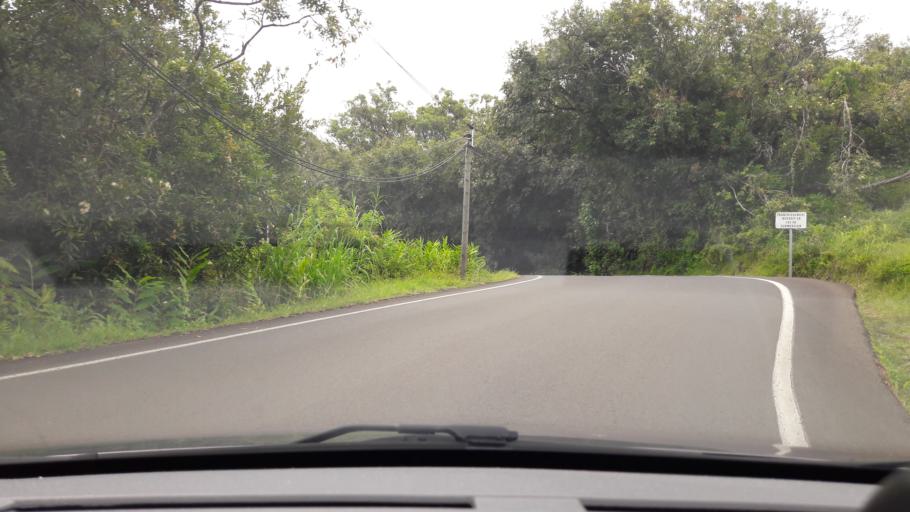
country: RE
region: Reunion
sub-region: Reunion
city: Saint-Benoit
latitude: -21.0855
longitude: 55.6964
